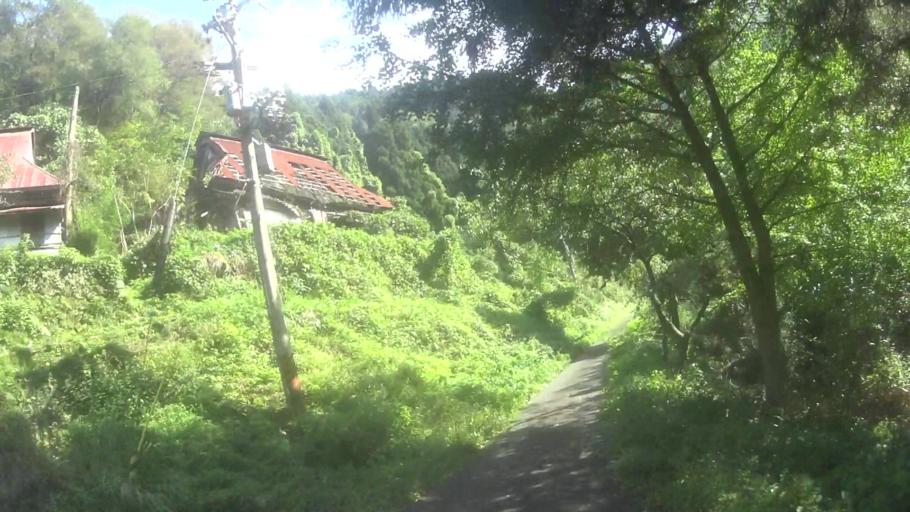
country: JP
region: Kyoto
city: Miyazu
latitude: 35.7149
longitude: 135.1665
